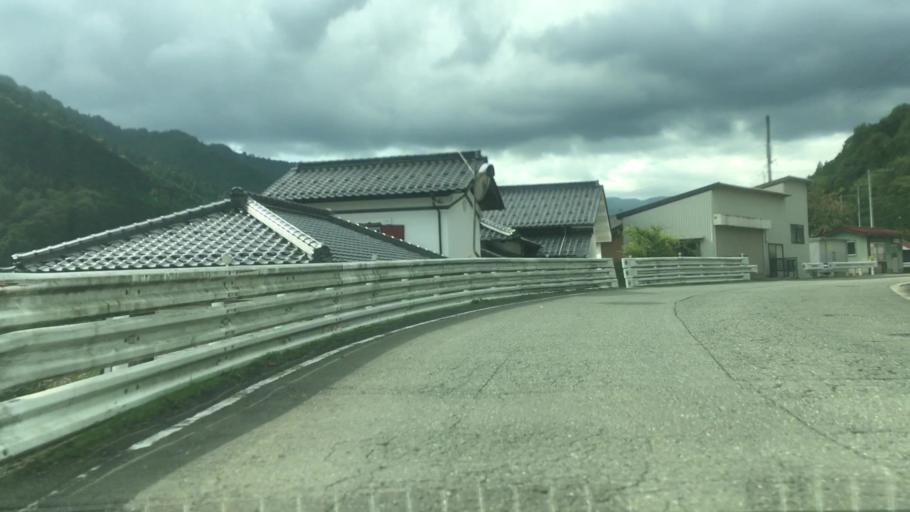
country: JP
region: Hyogo
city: Toyooka
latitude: 35.4096
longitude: 134.7481
